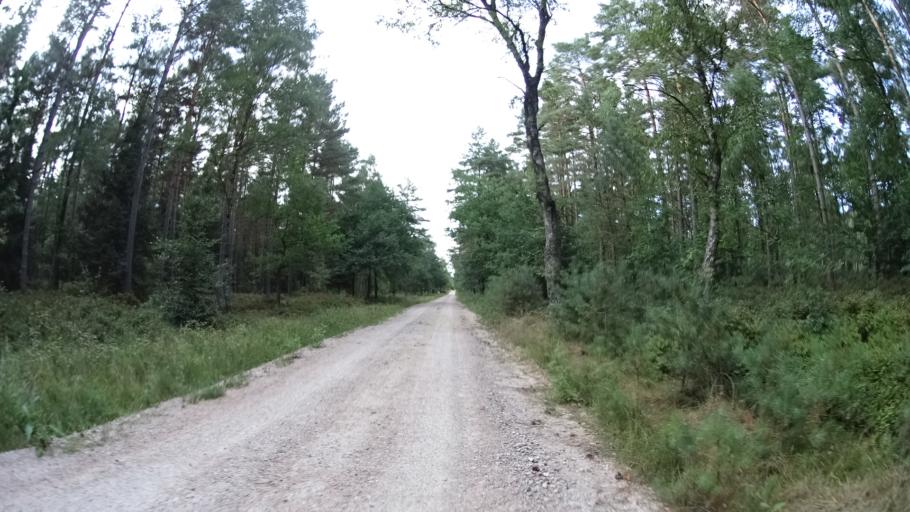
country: DE
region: Lower Saxony
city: Handeloh
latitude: 53.1864
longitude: 9.8840
